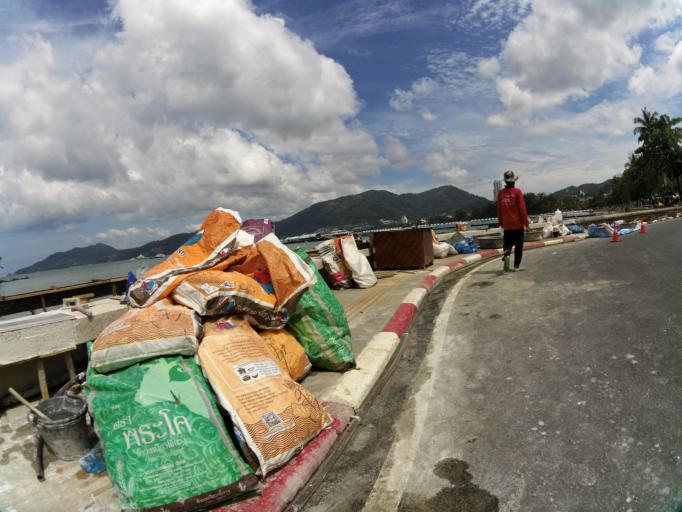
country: TH
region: Phuket
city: Patong
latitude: 7.8857
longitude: 98.2876
